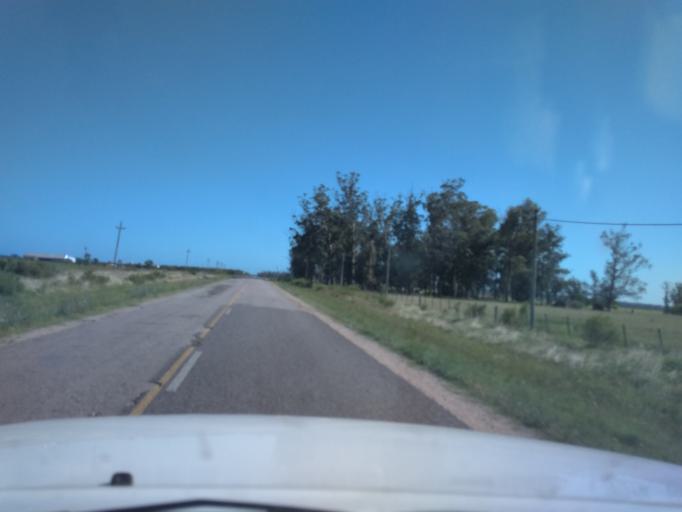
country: UY
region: Canelones
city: San Ramon
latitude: -34.1569
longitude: -55.9466
